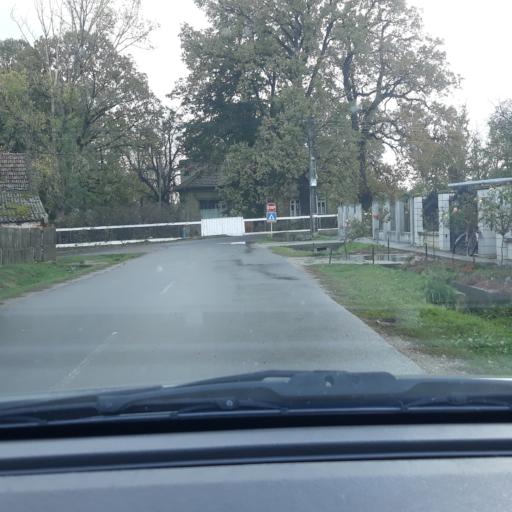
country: RO
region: Bihor
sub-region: Comuna Tarcea
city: Galospetreu
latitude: 47.4850
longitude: 22.2127
